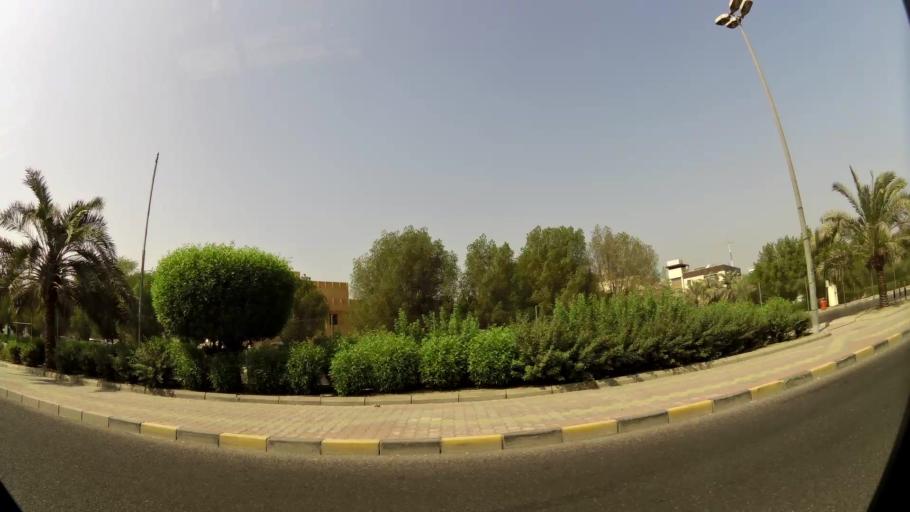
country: KW
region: Al Asimah
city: Ad Dasmah
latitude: 29.3594
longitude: 48.0059
